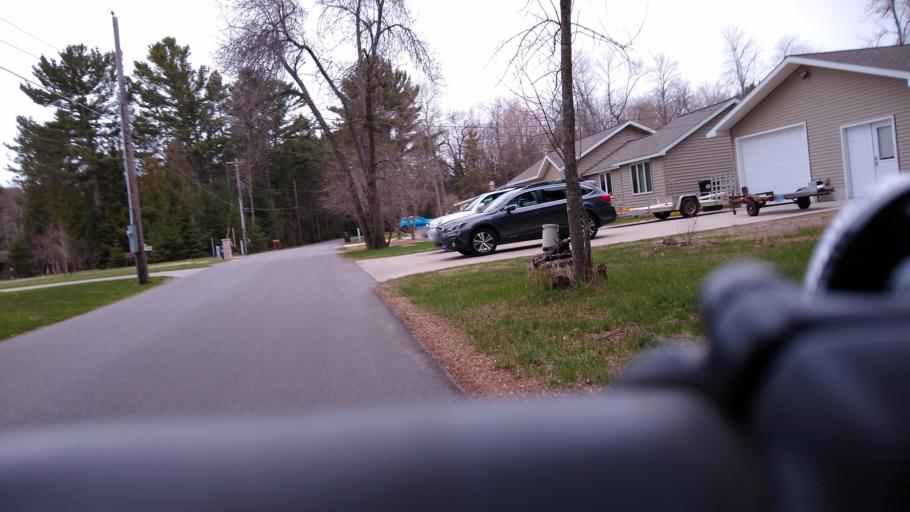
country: US
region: Michigan
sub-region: Delta County
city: Escanaba
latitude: 45.7015
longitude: -87.0971
